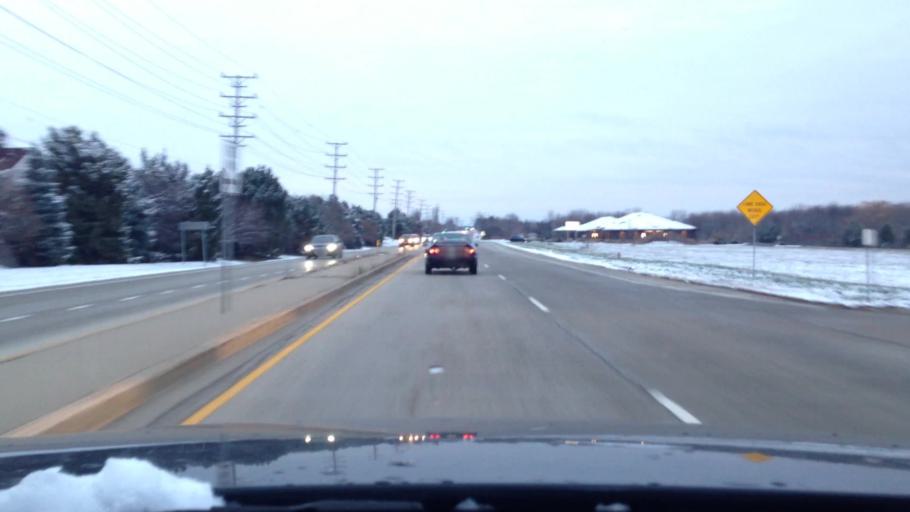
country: US
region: Illinois
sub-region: McHenry County
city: Huntley
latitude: 42.1774
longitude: -88.3836
